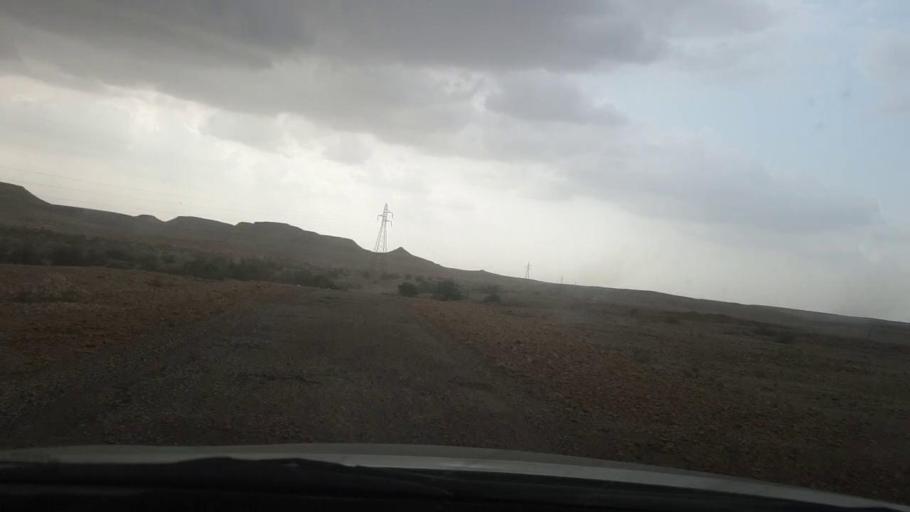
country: PK
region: Sindh
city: Khairpur
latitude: 27.4428
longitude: 68.9624
